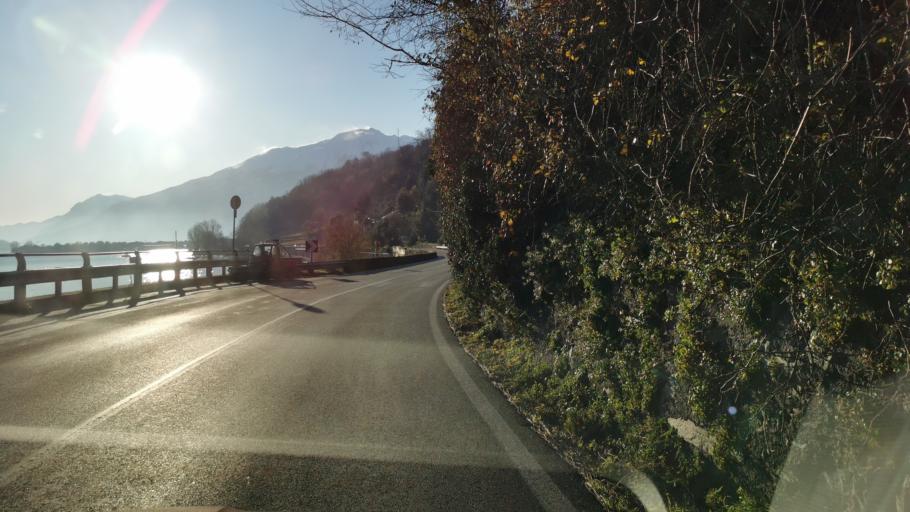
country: IT
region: Lombardy
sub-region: Provincia di Como
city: Trezzone
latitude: 46.1644
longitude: 9.3486
